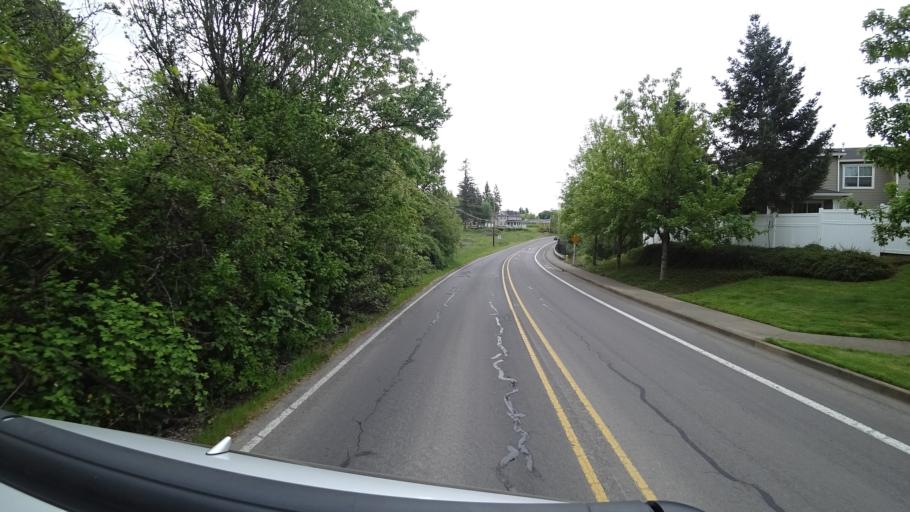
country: US
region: Oregon
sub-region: Washington County
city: Hillsboro
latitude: 45.5360
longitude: -122.9938
